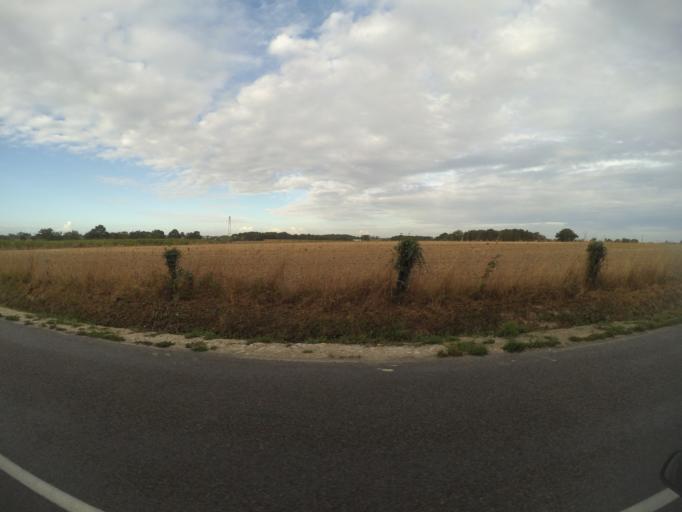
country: FR
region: Pays de la Loire
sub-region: Departement de la Loire-Atlantique
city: La Planche
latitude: 47.0277
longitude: -1.4215
